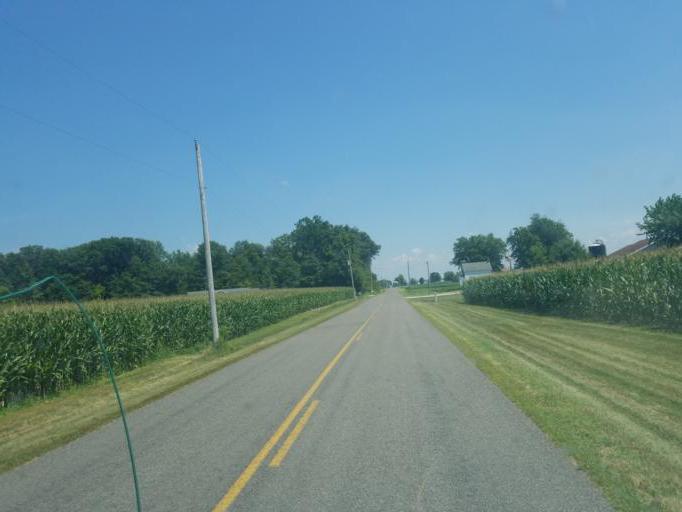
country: US
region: Ohio
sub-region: Shelby County
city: Botkins
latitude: 40.4822
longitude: -84.2127
